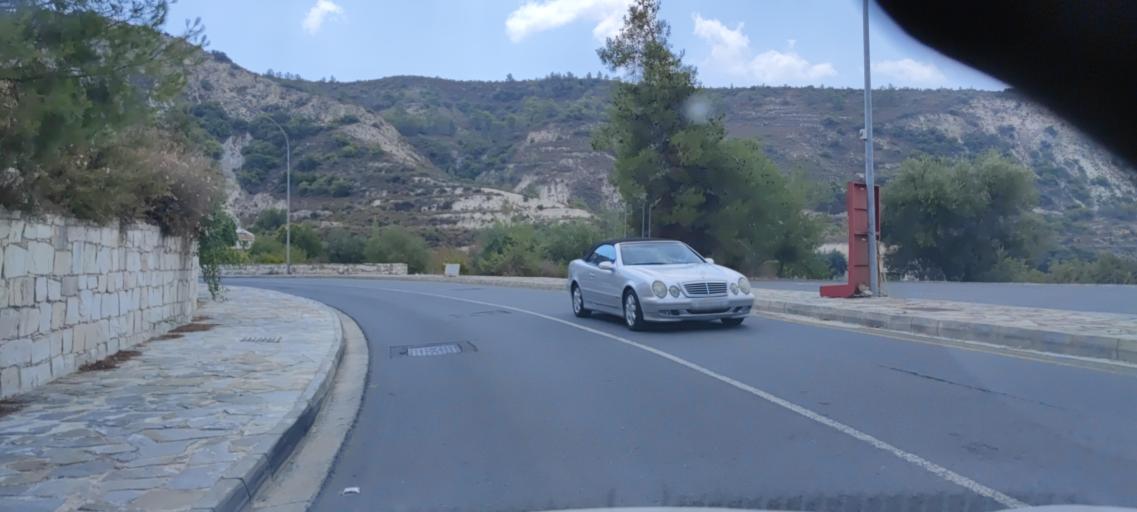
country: CY
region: Limassol
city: Pelendri
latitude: 34.8435
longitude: 32.9138
